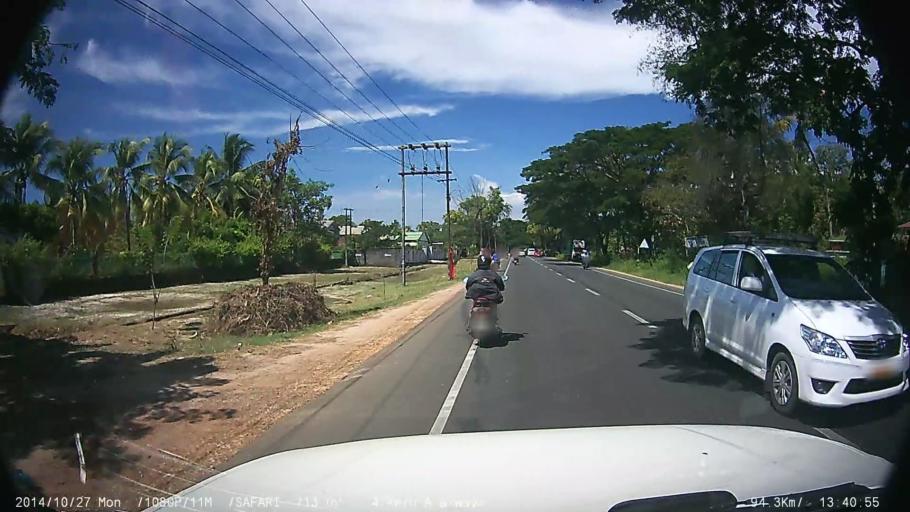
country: IN
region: Kerala
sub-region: Alappuzha
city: Shertallai
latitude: 9.6389
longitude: 76.3349
